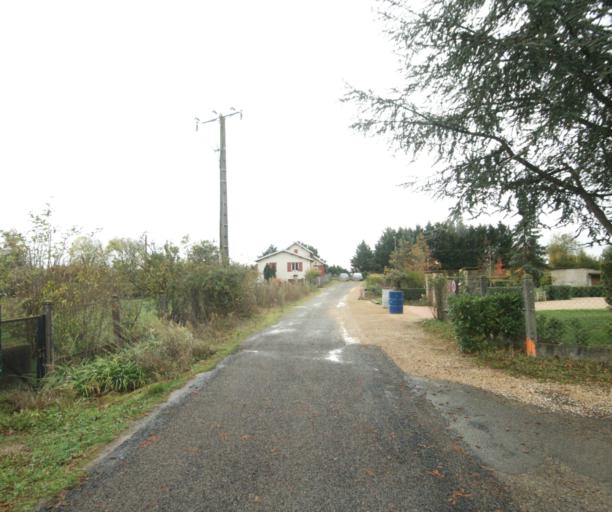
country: FR
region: Rhone-Alpes
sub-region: Departement de l'Ain
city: Pont-de-Vaux
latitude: 46.4731
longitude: 4.8953
